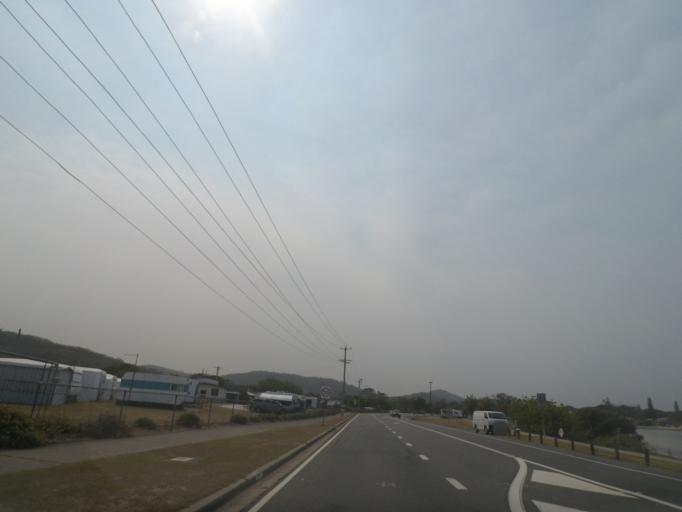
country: AU
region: New South Wales
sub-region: Tweed
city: Pottsville Beach
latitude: -28.3612
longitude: 153.5757
